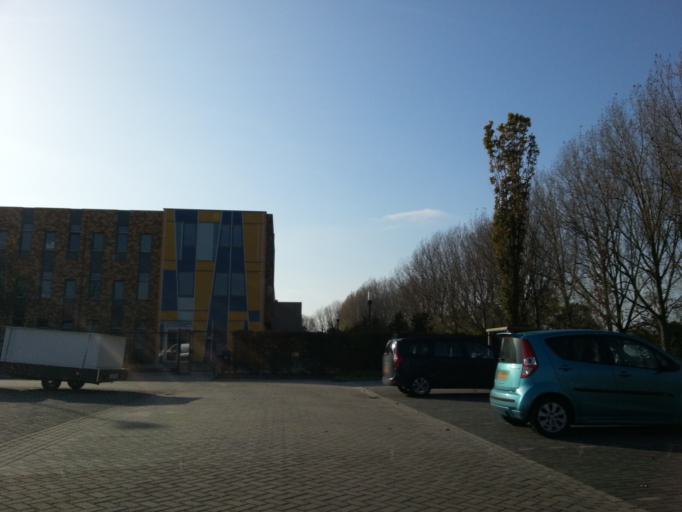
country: NL
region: South Holland
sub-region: Gemeente Pijnacker-Nootdorp
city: Pijnacker
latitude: 52.0248
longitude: 4.4204
